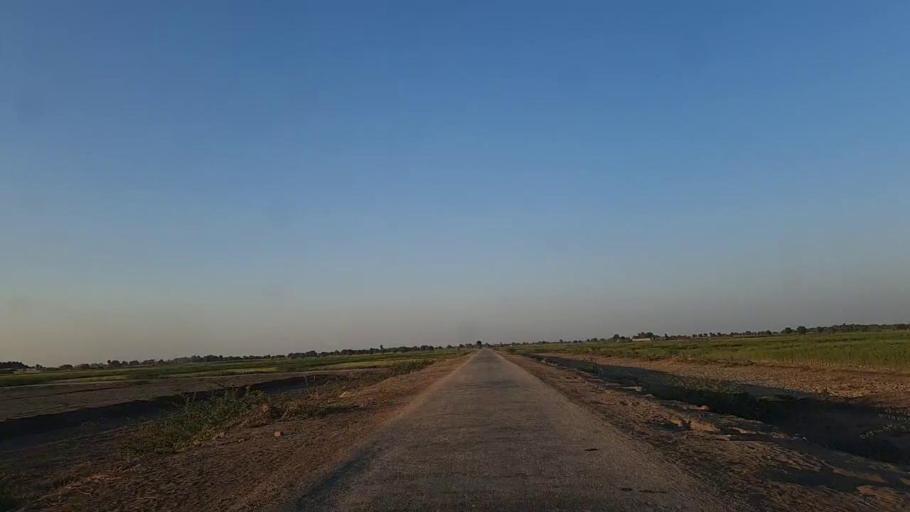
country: PK
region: Sindh
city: Naukot
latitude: 25.0218
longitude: 69.4168
